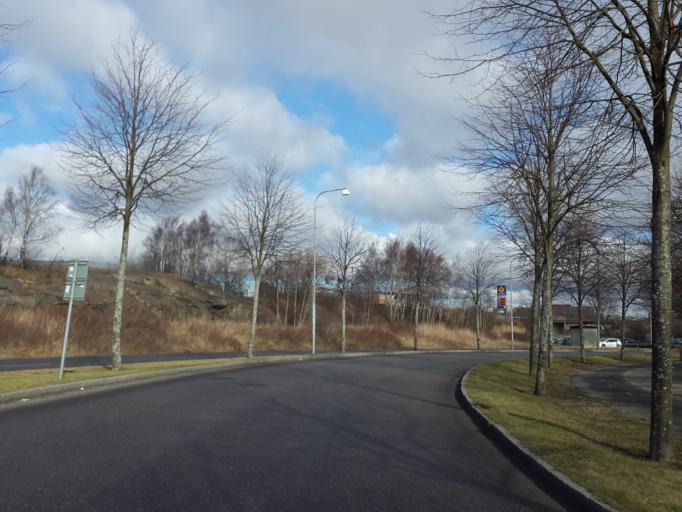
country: SE
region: Vaestra Goetaland
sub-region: Goteborg
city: Majorna
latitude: 57.7053
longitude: 11.9180
